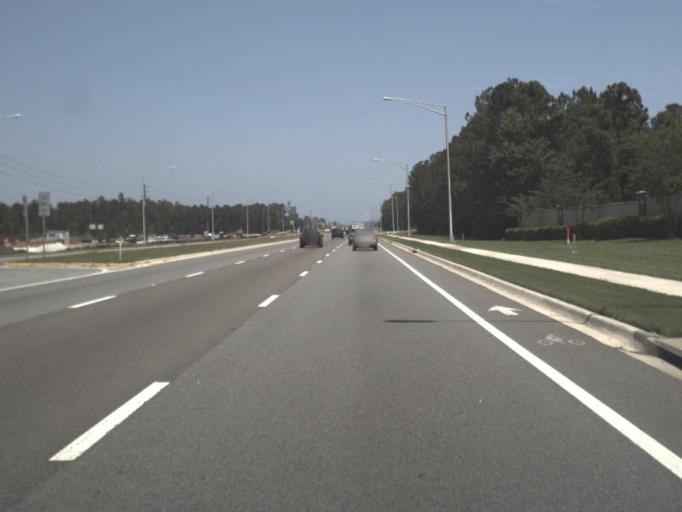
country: US
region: Florida
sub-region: Duval County
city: Jacksonville Beach
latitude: 30.2874
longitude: -81.4725
